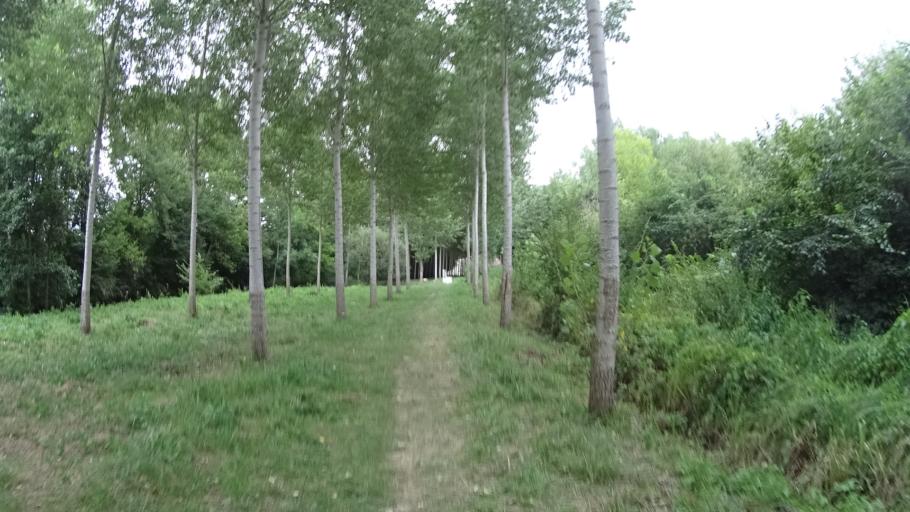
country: FR
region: Centre
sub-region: Departement du Loiret
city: Amilly
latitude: 47.9520
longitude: 2.7832
